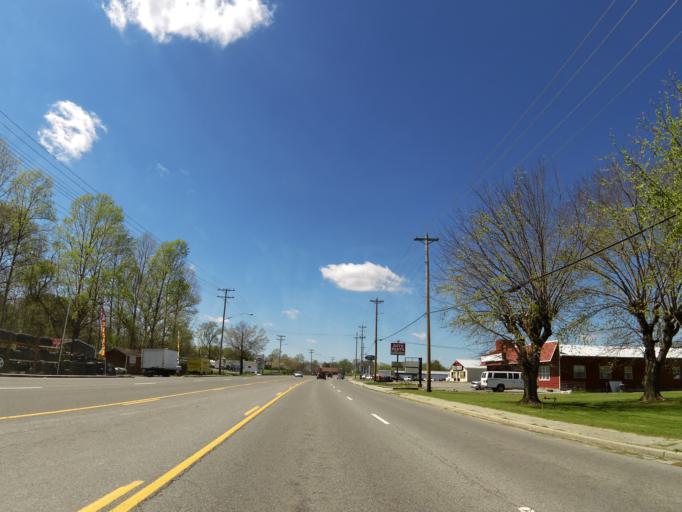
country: US
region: Tennessee
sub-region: DeKalb County
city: Smithville
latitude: 35.9597
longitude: -85.8368
